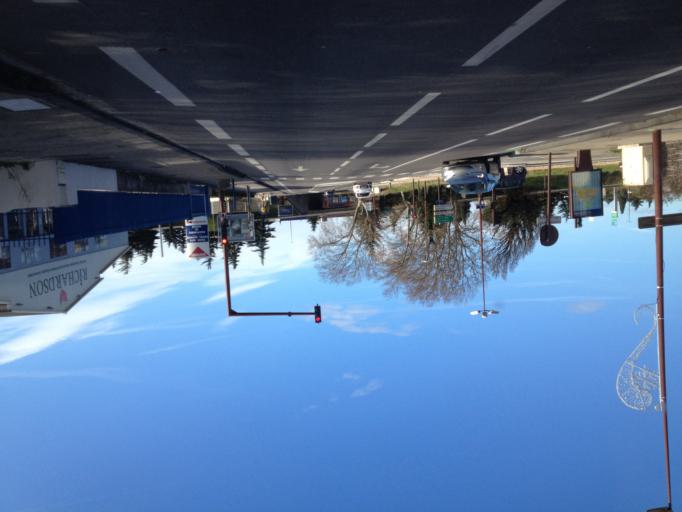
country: FR
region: Provence-Alpes-Cote d'Azur
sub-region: Departement du Vaucluse
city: Avignon
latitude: 43.9401
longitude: 4.8300
